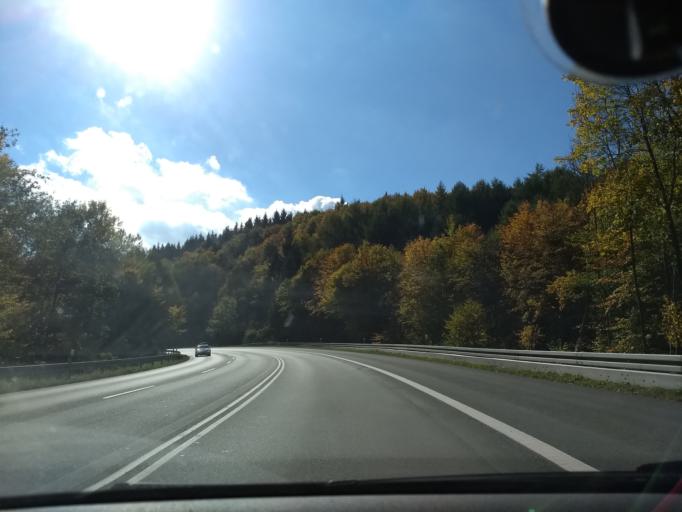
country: DE
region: North Rhine-Westphalia
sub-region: Regierungsbezirk Arnsberg
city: Meschede
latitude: 51.3837
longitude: 8.2945
